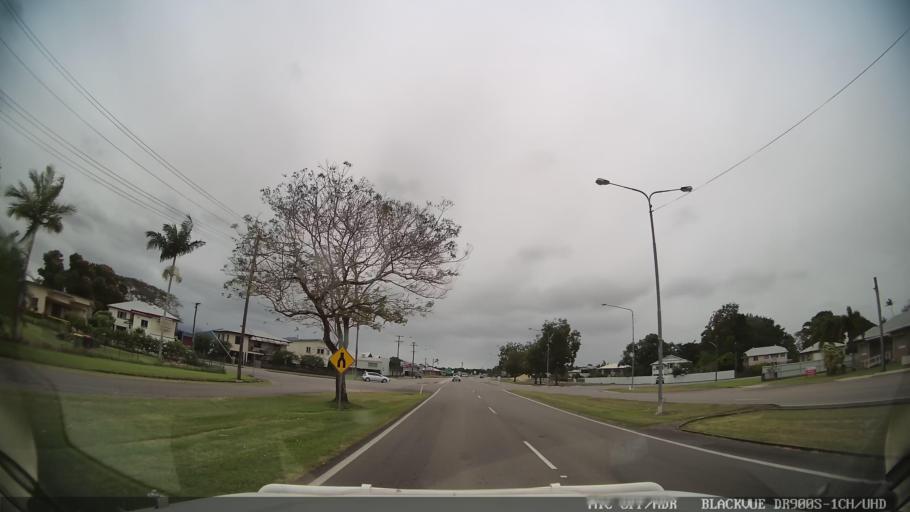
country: AU
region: Queensland
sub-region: Hinchinbrook
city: Ingham
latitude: -18.6438
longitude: 146.1627
